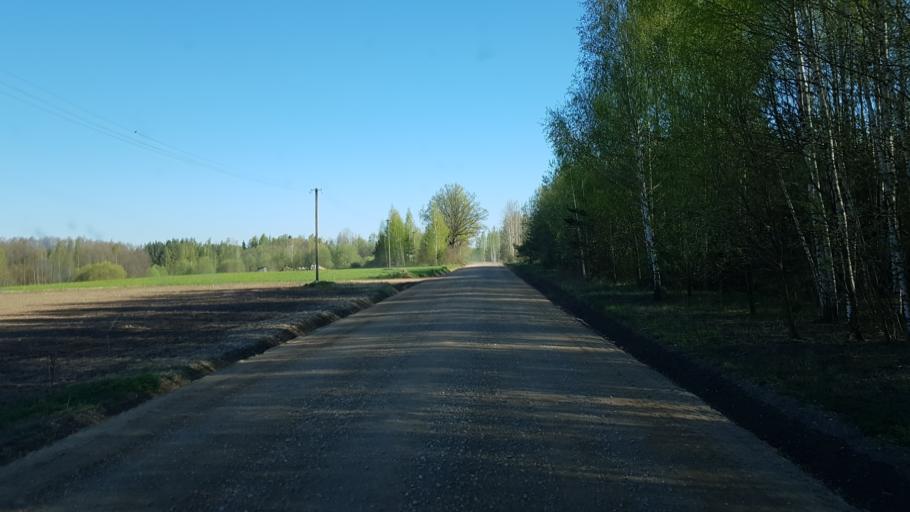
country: EE
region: Polvamaa
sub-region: Polva linn
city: Polva
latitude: 58.1109
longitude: 27.2393
